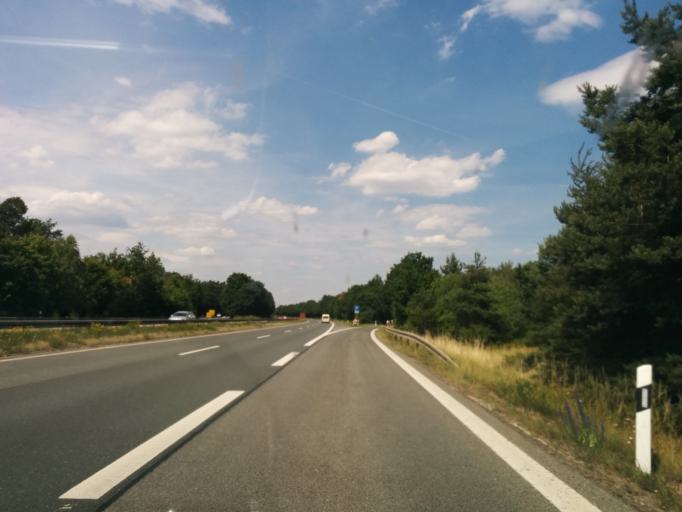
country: DE
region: Bavaria
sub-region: Regierungsbezirk Mittelfranken
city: Rednitzhembach
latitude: 49.3130
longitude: 11.0855
